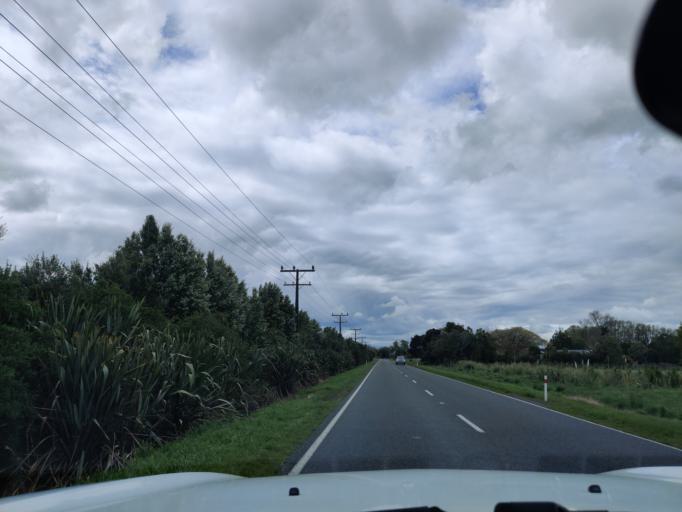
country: NZ
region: Manawatu-Wanganui
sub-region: Palmerston North City
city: Palmerston North
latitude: -40.2450
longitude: 175.5497
